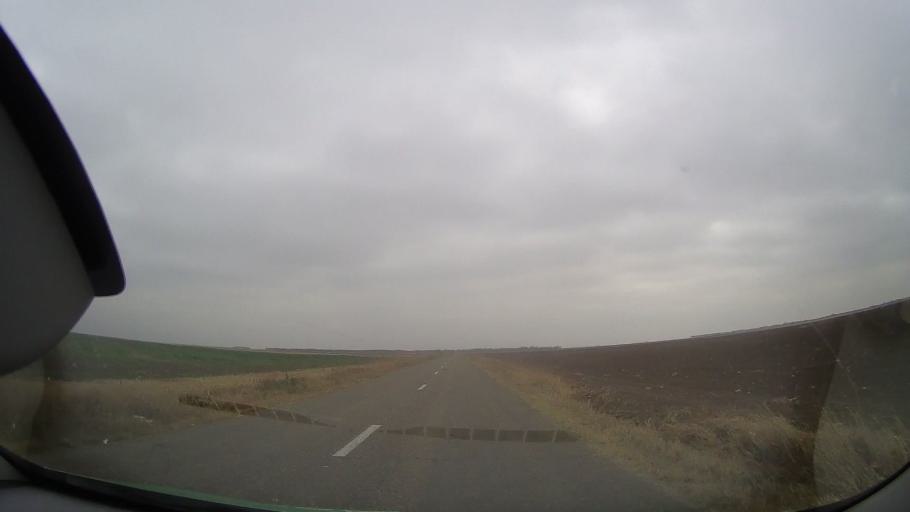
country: RO
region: Buzau
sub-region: Comuna Bradeanu
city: Bradeanu
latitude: 44.9001
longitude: 26.8722
